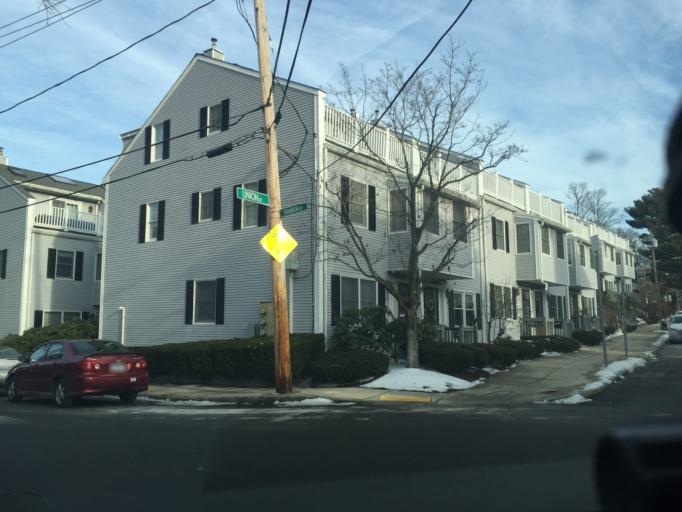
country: US
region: Massachusetts
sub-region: Norfolk County
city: Brookline
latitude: 42.3456
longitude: -71.1503
